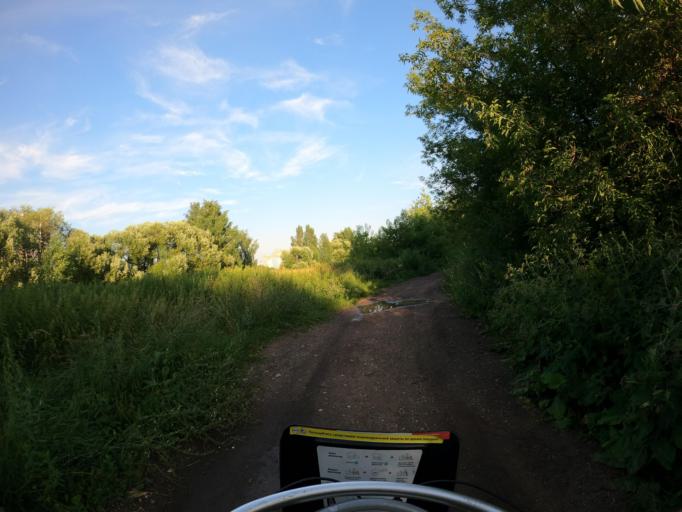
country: RU
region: Moscow
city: Strogino
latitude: 55.8237
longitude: 37.4062
